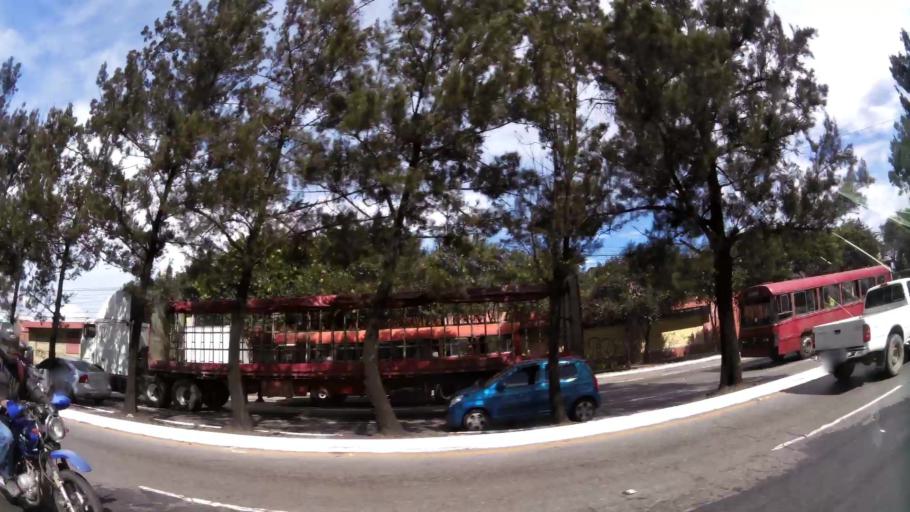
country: GT
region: Guatemala
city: Guatemala City
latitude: 14.6321
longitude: -90.5581
